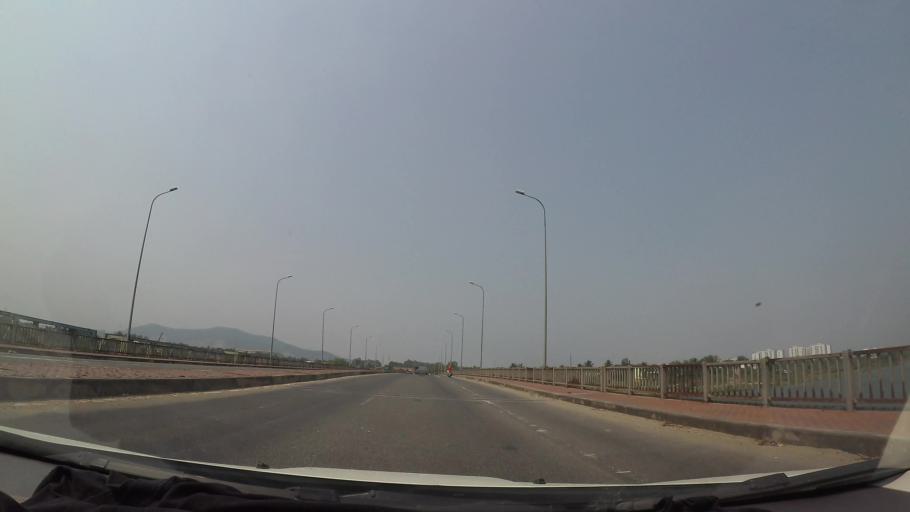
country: VN
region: Da Nang
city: Cam Le
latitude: 15.9985
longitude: 108.1913
